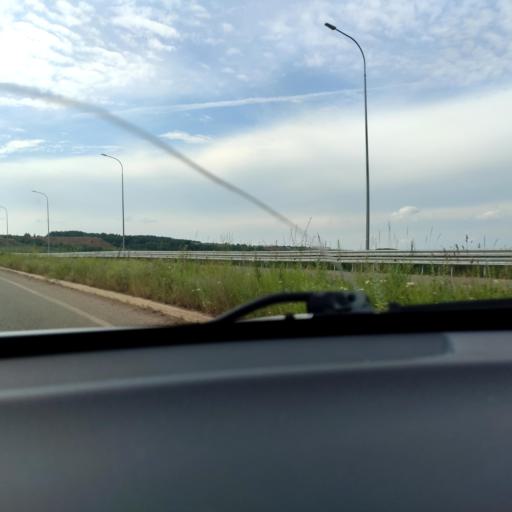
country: RU
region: Tatarstan
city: Sviyazhsk
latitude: 55.7451
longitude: 48.7705
